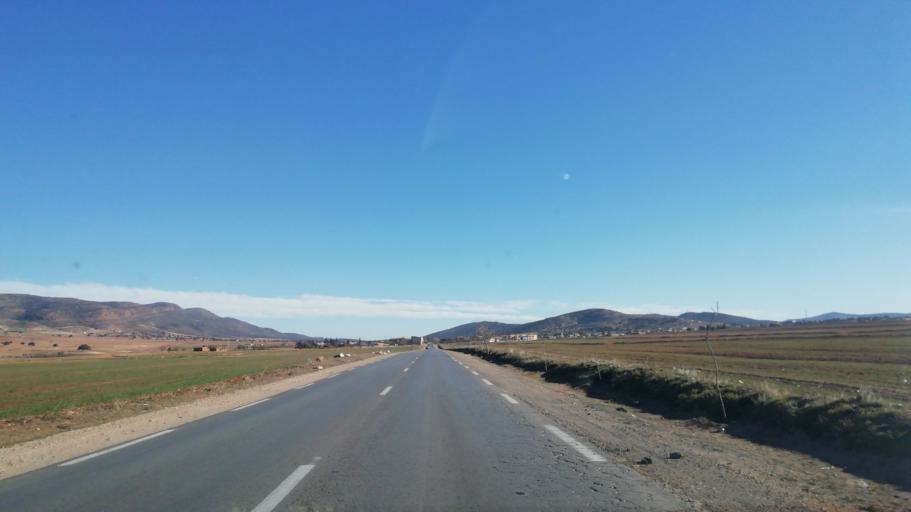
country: DZ
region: Tlemcen
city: Sebdou
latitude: 34.6684
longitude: -1.2816
